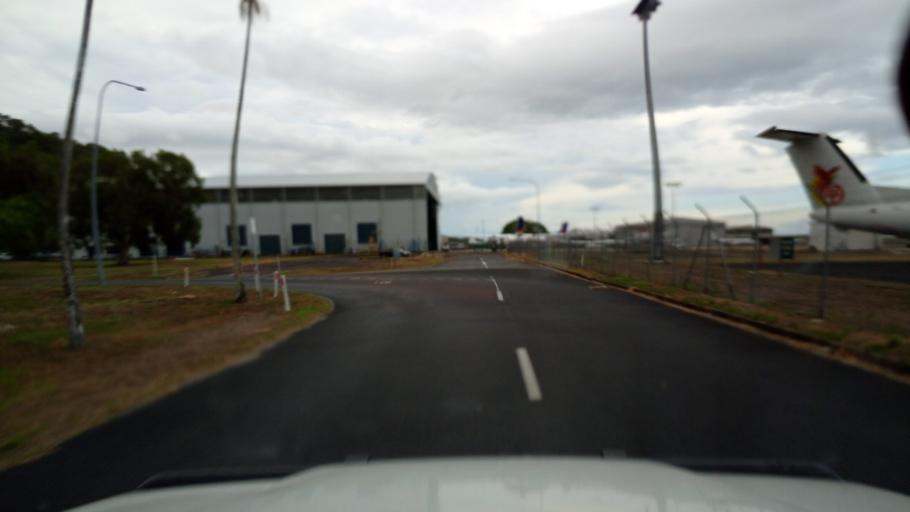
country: AU
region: Queensland
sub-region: Cairns
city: Cairns
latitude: -16.8851
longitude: 145.7494
